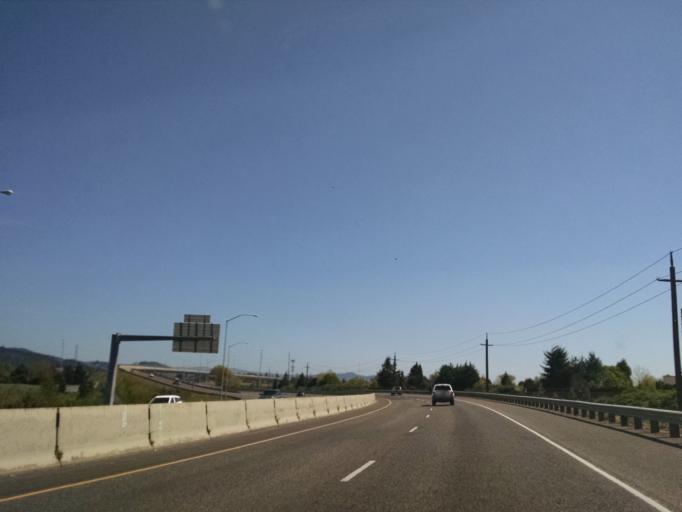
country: US
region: Oregon
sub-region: Lane County
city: Eugene
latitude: 44.0847
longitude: -123.0576
